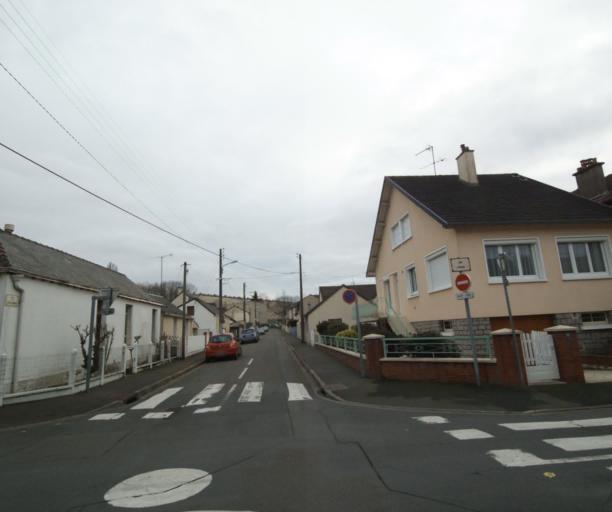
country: FR
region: Pays de la Loire
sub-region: Departement de la Sarthe
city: Le Mans
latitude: 47.9757
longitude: 0.2084
